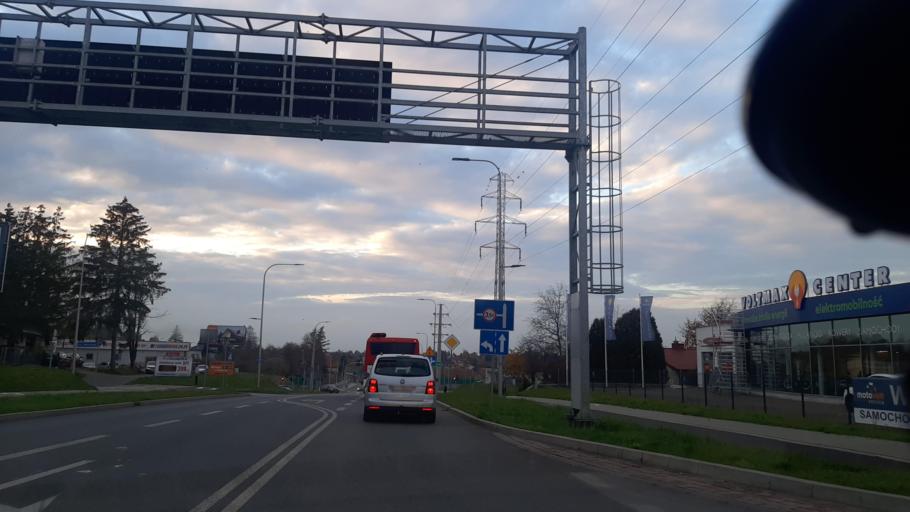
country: PL
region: Lublin Voivodeship
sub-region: Powiat lubelski
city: Lublin
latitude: 51.2512
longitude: 22.5087
